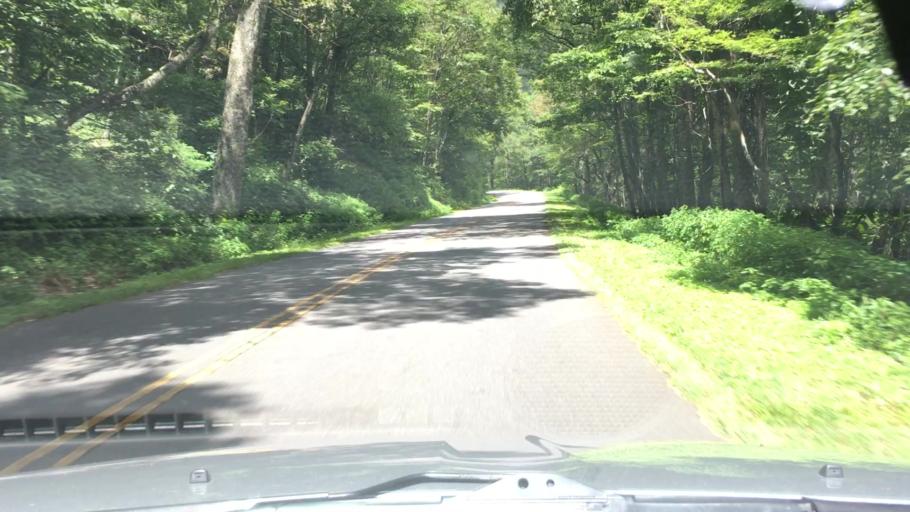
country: US
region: North Carolina
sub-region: Buncombe County
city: Swannanoa
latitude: 35.6719
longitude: -82.4437
